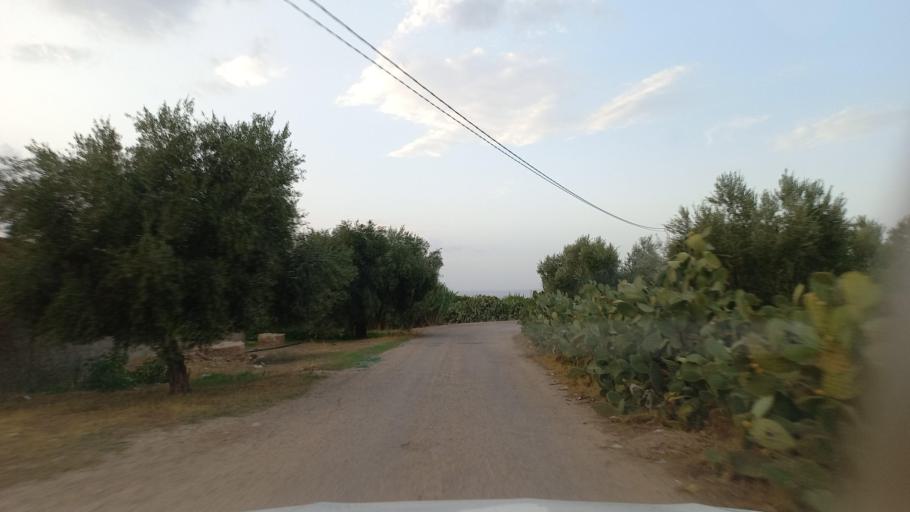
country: TN
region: Al Qasrayn
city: Kasserine
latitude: 35.2796
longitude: 9.0505
